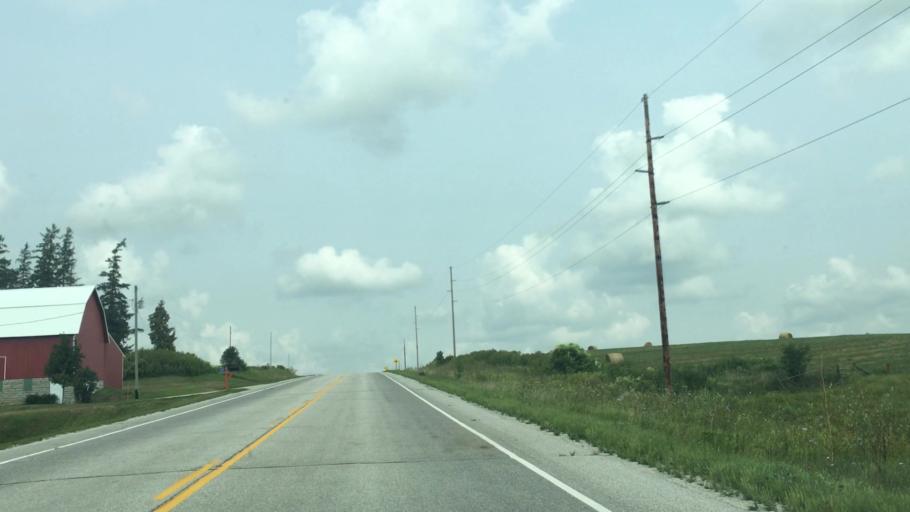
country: US
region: Minnesota
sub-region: Fillmore County
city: Harmony
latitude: 43.5768
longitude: -91.9298
